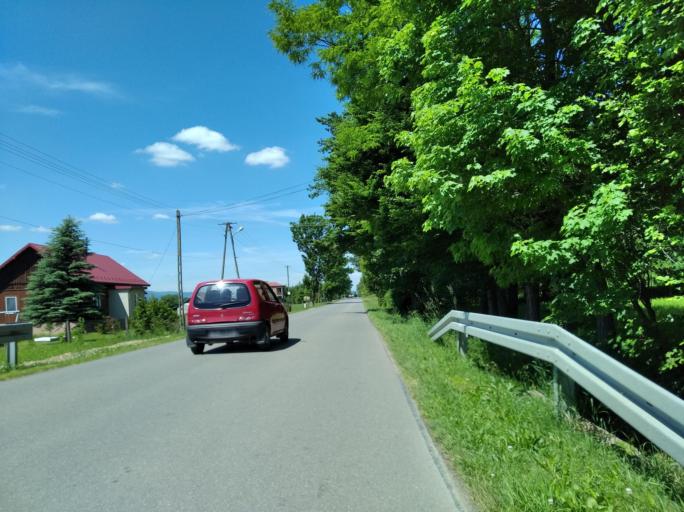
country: PL
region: Subcarpathian Voivodeship
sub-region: Powiat jasielski
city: Nowy Zmigrod
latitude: 49.6176
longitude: 21.5689
